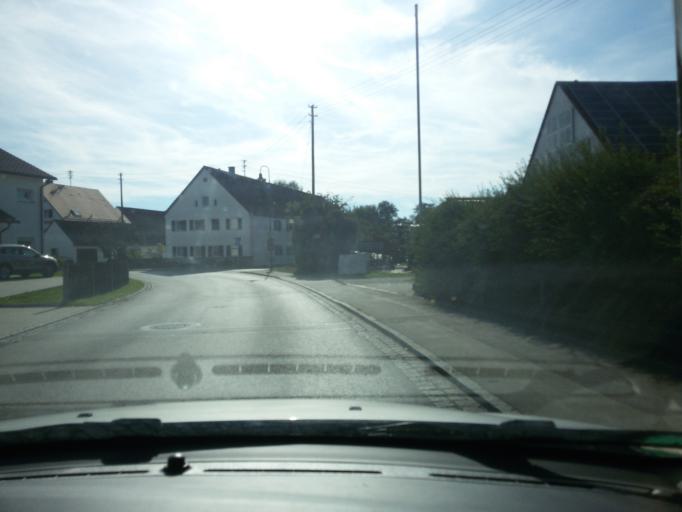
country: DE
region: Bavaria
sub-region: Swabia
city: Kutzenhausen
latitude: 48.3426
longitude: 10.6939
